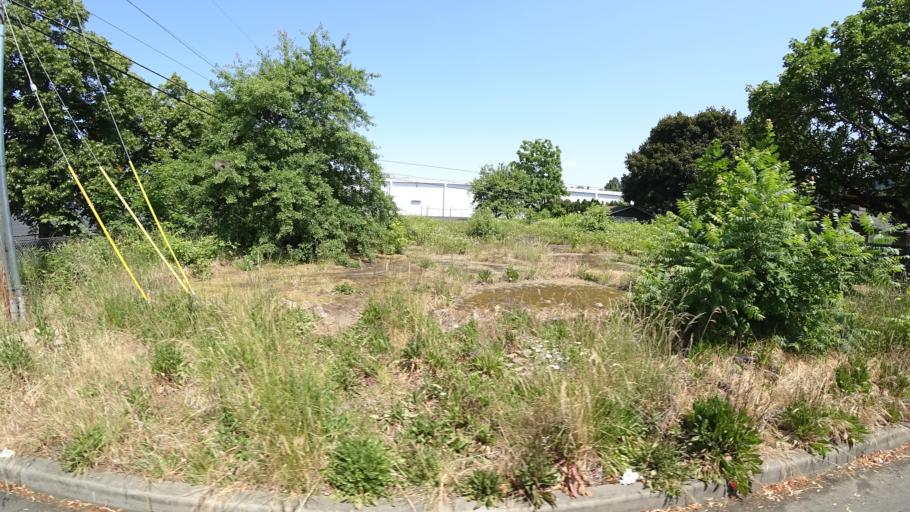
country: US
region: Oregon
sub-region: Multnomah County
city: Lents
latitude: 45.4460
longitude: -122.5766
